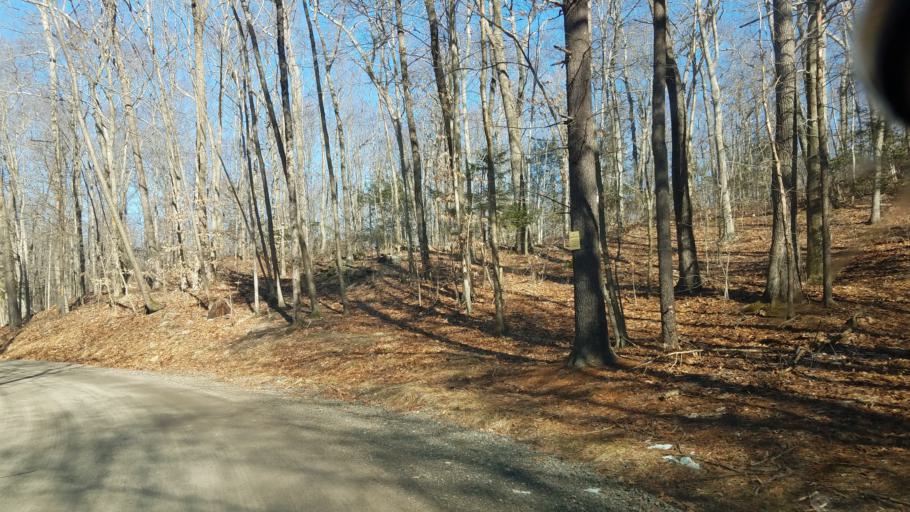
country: US
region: Connecticut
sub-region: New Haven County
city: Heritage Village
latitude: 41.5108
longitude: -73.2831
